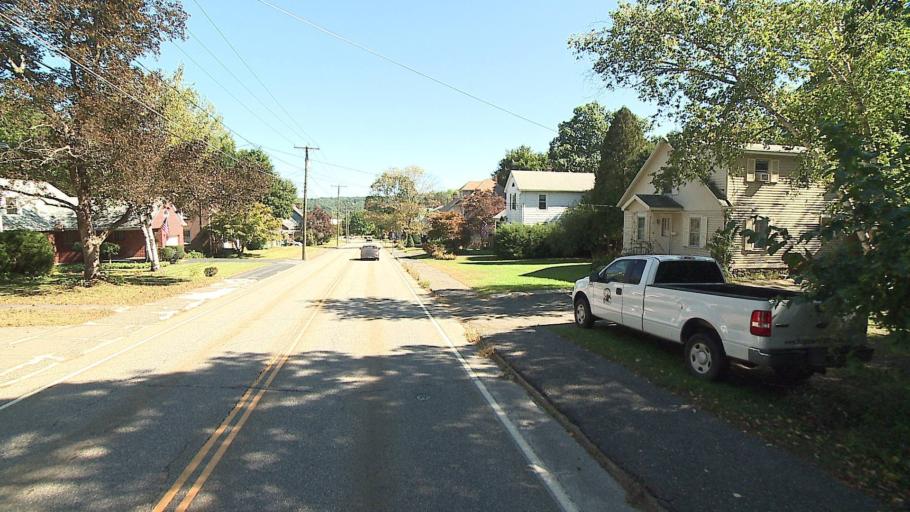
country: US
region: Connecticut
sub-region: Litchfield County
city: Torrington
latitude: 41.7898
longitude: -73.1281
